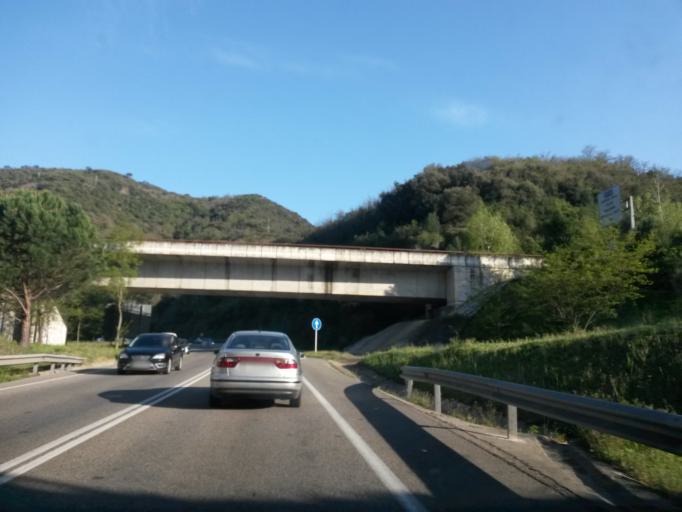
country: ES
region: Catalonia
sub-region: Provincia de Girona
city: Sant Julia de Ramis
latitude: 42.0229
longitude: 2.8502
